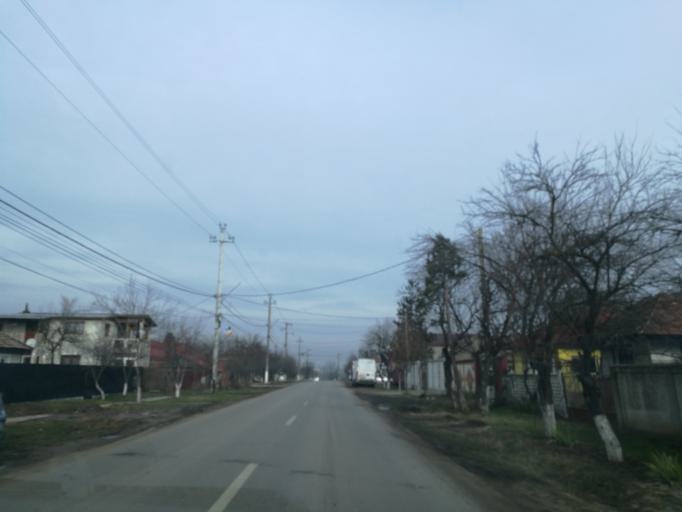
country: RO
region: Ilfov
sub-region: Comuna Moara Vlasiei
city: Caciulati
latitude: 44.6297
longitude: 26.1772
